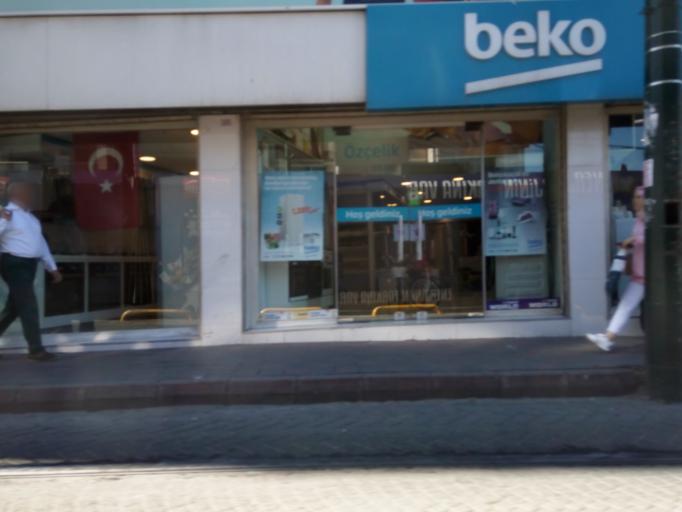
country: TR
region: Istanbul
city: Zeytinburnu
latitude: 41.0040
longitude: 28.9039
